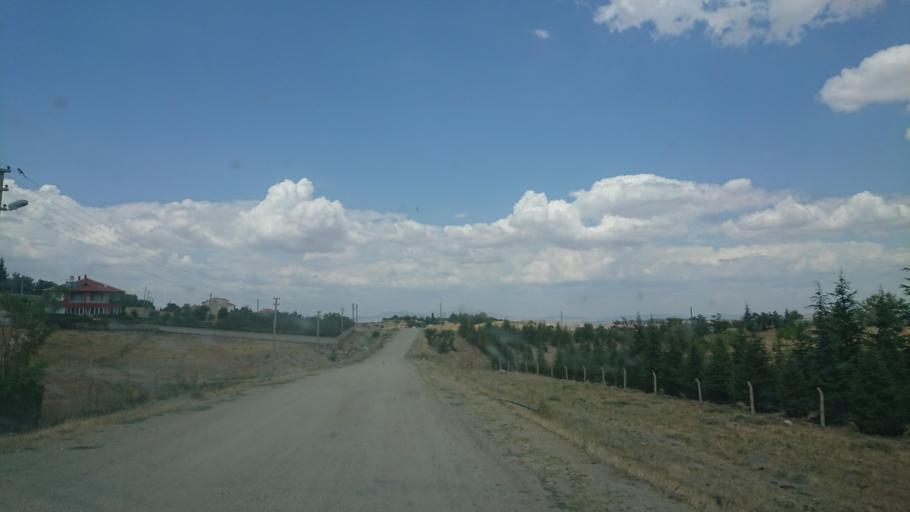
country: TR
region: Aksaray
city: Sariyahsi
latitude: 38.9511
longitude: 33.8822
